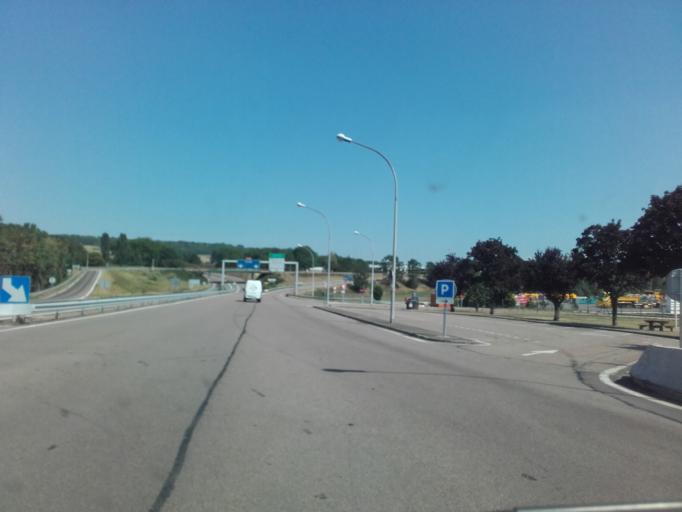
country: FR
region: Bourgogne
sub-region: Departement de la Cote-d'Or
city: Pouilly-en-Auxois
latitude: 47.2525
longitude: 4.5615
